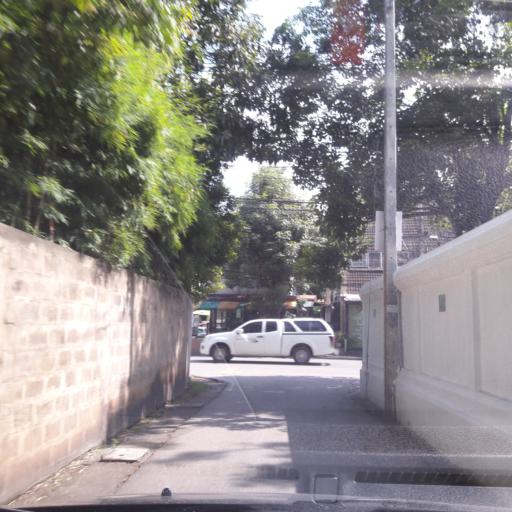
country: TH
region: Chiang Mai
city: Chiang Mai
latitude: 18.7815
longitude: 99.0010
